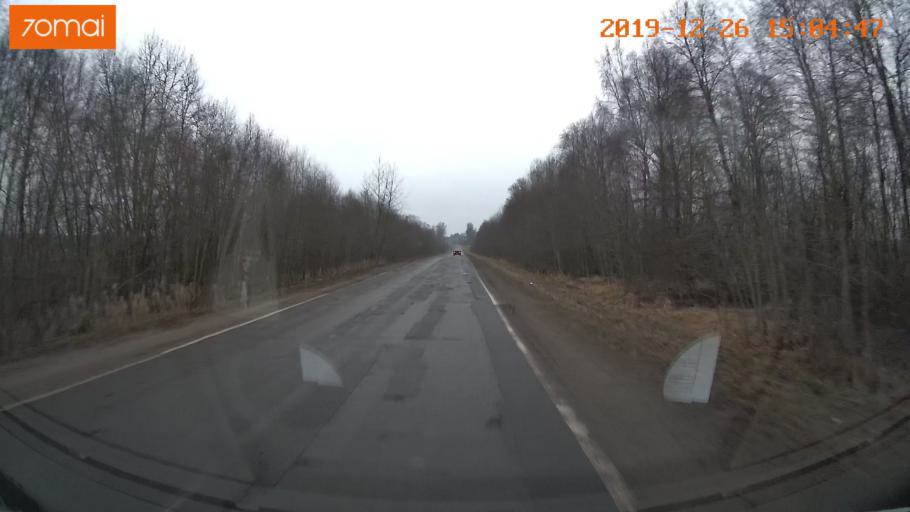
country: RU
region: Jaroslavl
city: Rybinsk
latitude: 58.1962
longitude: 38.8581
